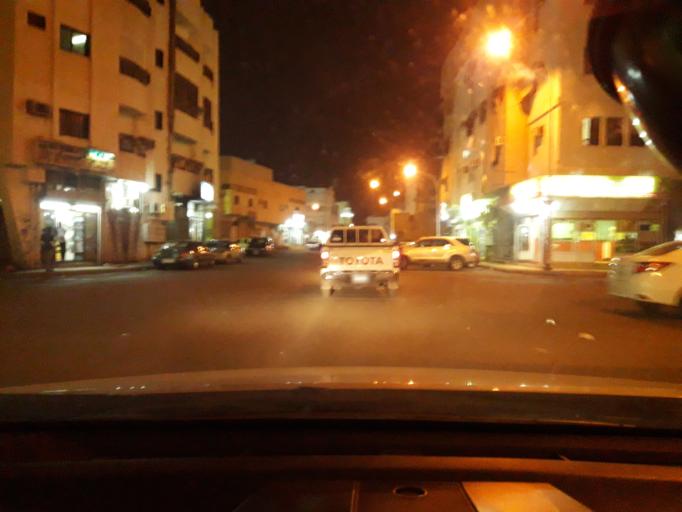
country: SA
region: Al Madinah al Munawwarah
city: Medina
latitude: 24.4656
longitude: 39.6288
